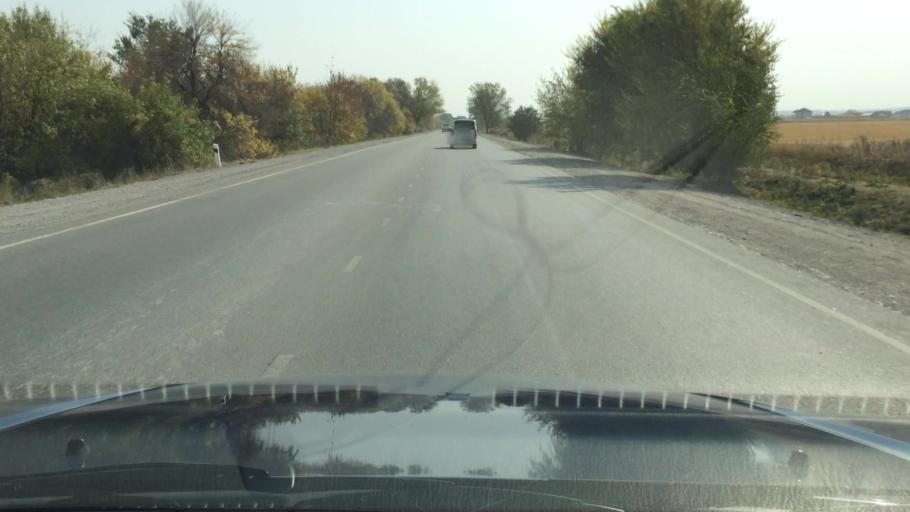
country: KG
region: Chuy
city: Lebedinovka
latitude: 42.9285
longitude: 74.6948
